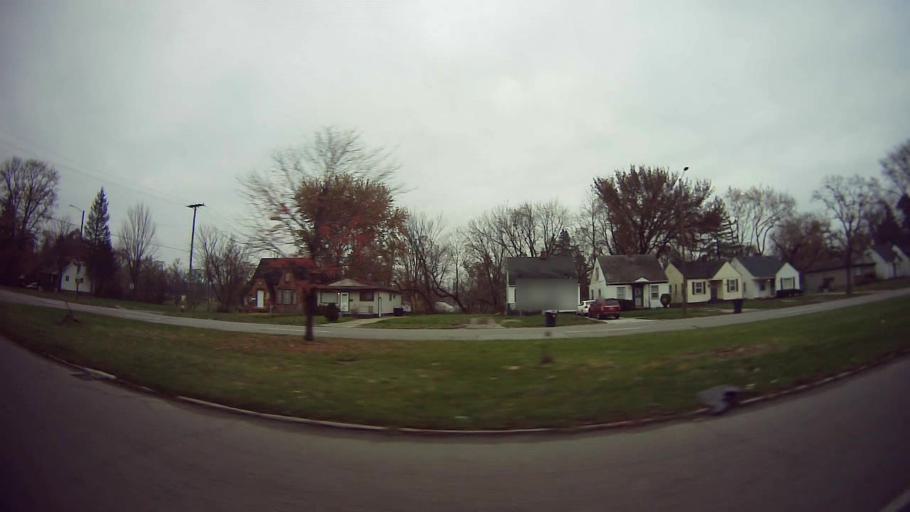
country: US
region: Michigan
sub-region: Wayne County
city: Redford
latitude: 42.3951
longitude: -83.2568
